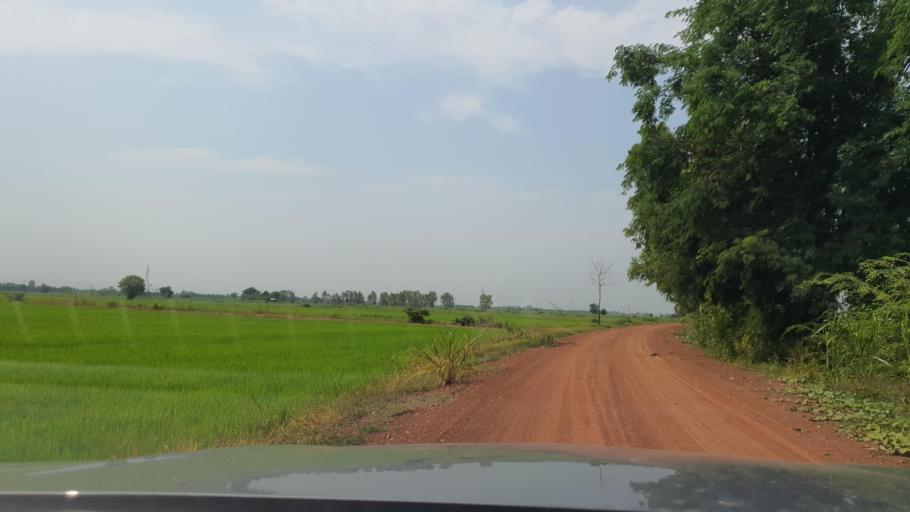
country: TH
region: Phitsanulok
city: Bang Rakam
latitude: 16.7921
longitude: 100.1092
